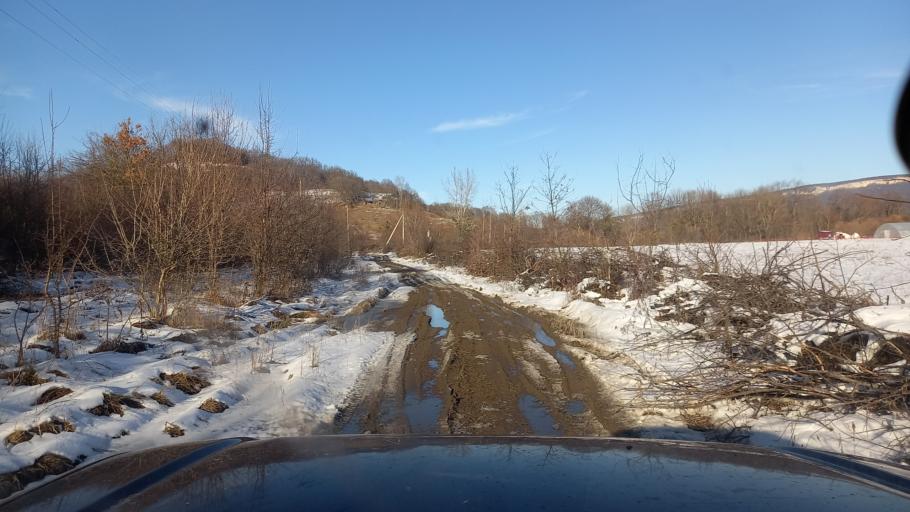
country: RU
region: Adygeya
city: Kamennomostskiy
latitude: 44.2016
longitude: 40.1507
